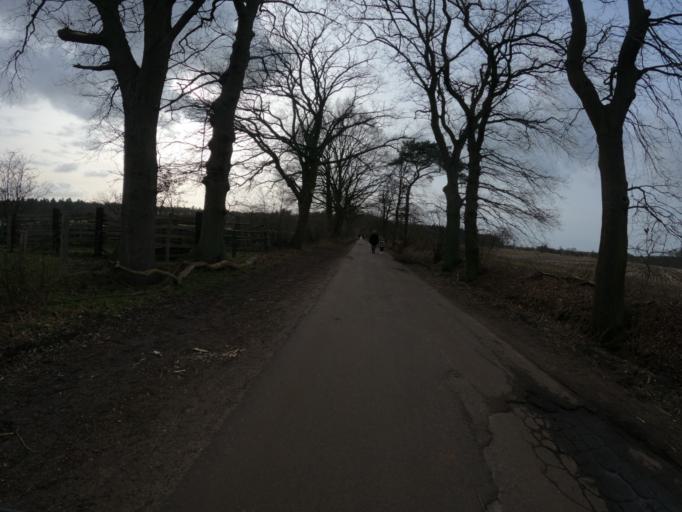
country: DE
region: Schleswig-Holstein
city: Rellingen
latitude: 53.6058
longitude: 9.7767
